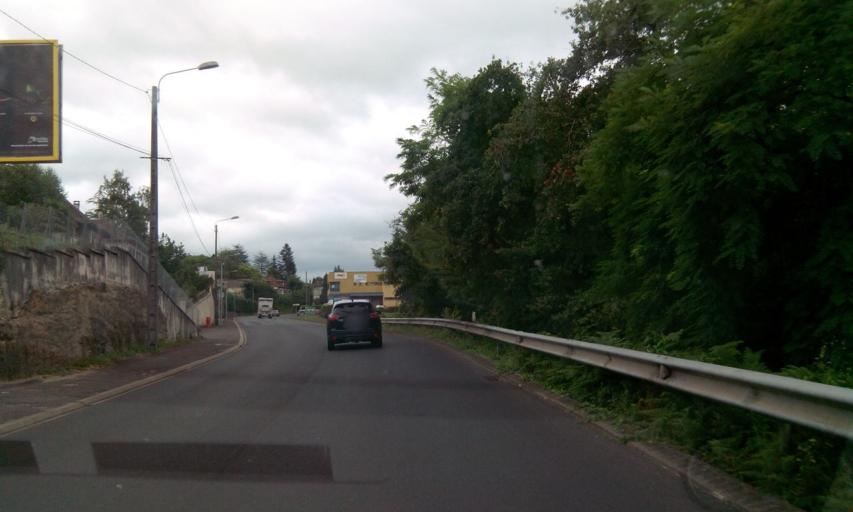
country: FR
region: Limousin
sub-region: Departement de la Correze
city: Brive-la-Gaillarde
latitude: 45.1451
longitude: 1.5477
